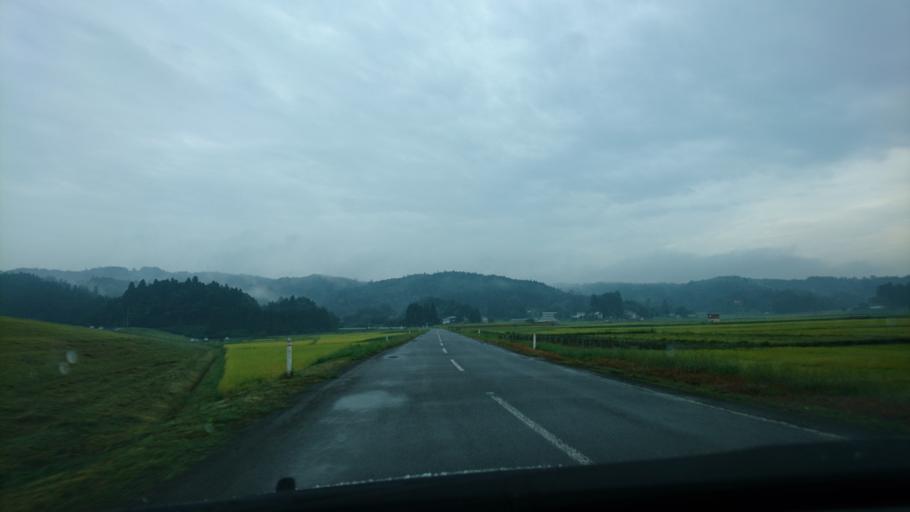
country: JP
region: Iwate
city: Ichinoseki
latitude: 38.8835
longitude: 141.2585
